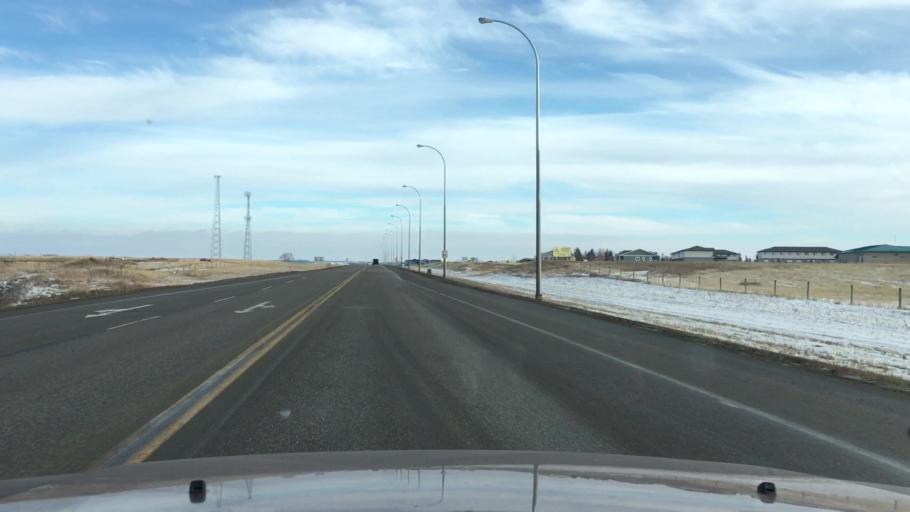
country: CA
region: Saskatchewan
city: Pilot Butte
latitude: 50.4856
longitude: -104.4333
